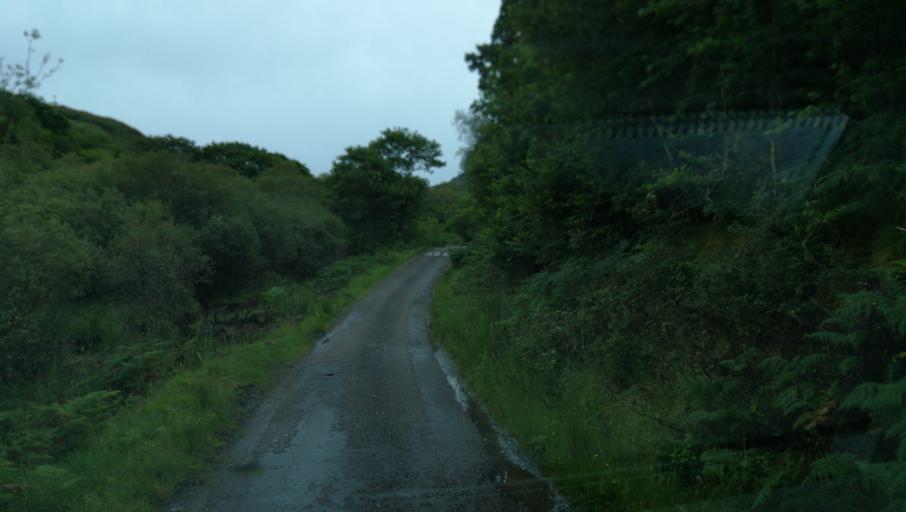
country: GB
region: Scotland
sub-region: Argyll and Bute
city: Isle Of Mull
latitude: 56.7198
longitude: -6.1688
